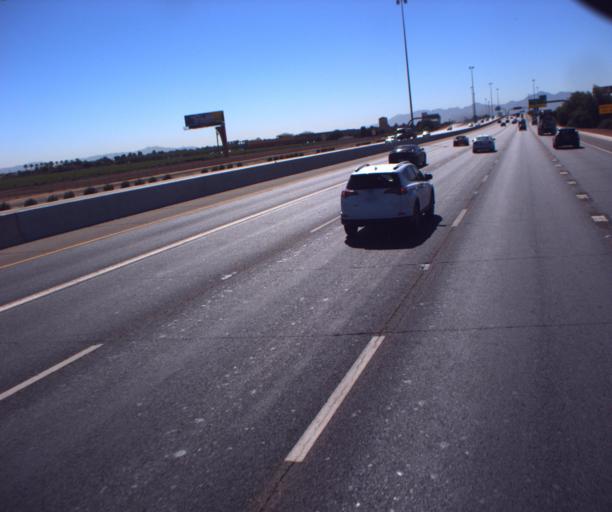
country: US
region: Arizona
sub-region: Maricopa County
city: Tolleson
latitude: 33.5163
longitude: -112.2693
